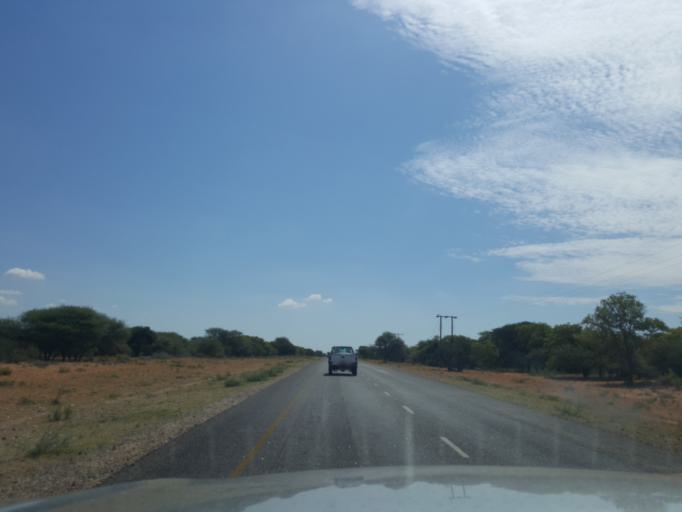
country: BW
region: Kweneng
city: Letlhakeng
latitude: -24.1243
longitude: 25.1006
